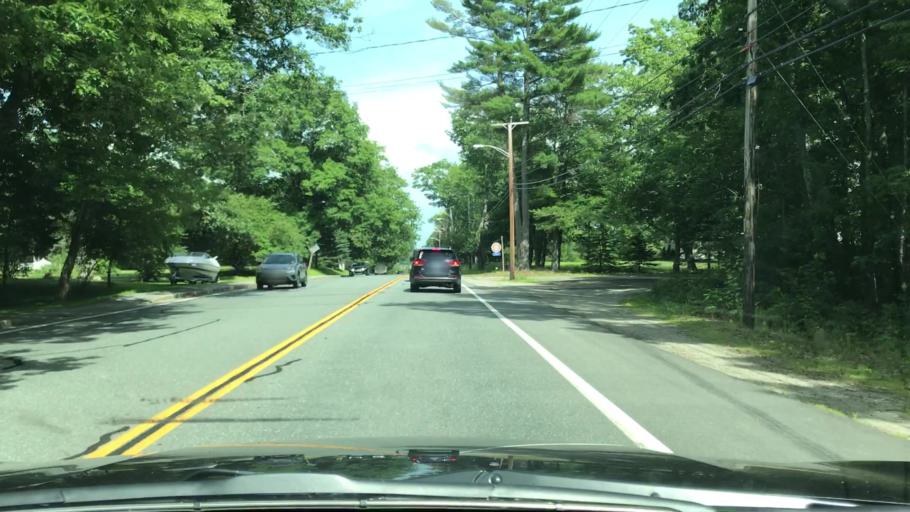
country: US
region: Maine
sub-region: Hancock County
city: Ellsworth
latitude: 44.5391
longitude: -68.4369
